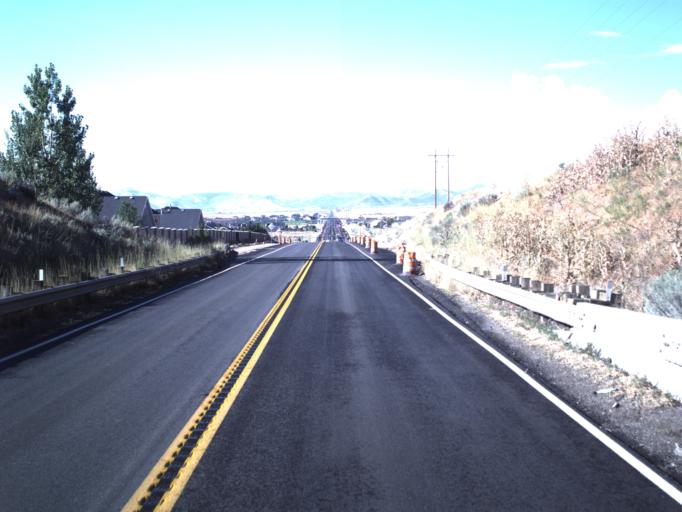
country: US
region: Utah
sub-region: Salt Lake County
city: Oquirrh
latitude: 40.6154
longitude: -112.0545
